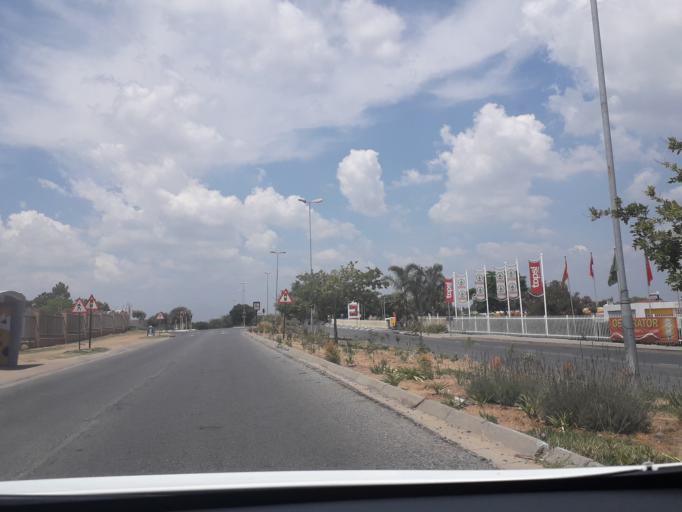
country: ZA
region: Gauteng
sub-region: City of Johannesburg Metropolitan Municipality
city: Midrand
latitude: -26.0365
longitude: 28.0805
